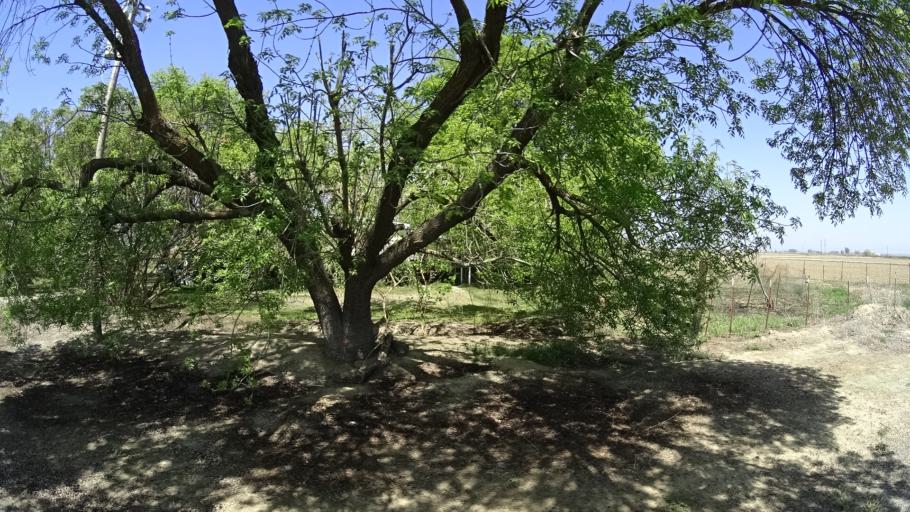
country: US
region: California
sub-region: Glenn County
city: Willows
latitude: 39.5238
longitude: -122.1157
